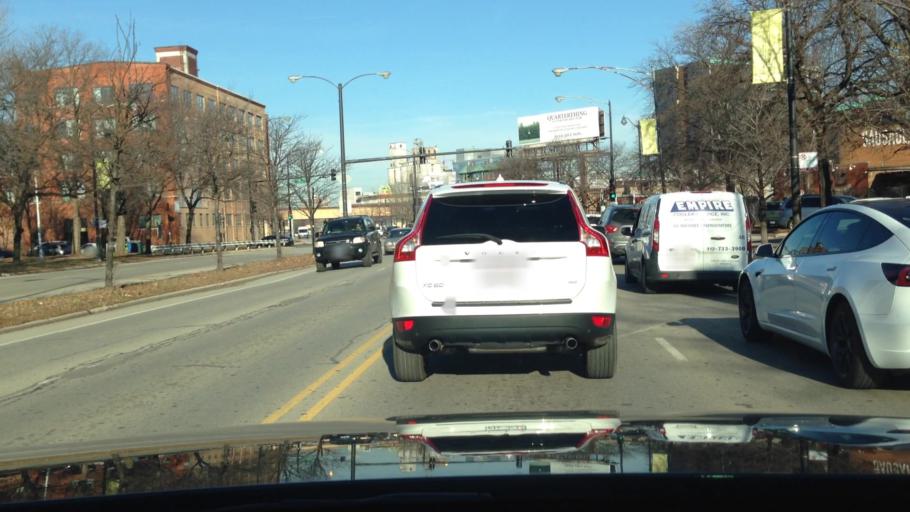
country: US
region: Illinois
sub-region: Cook County
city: Chicago
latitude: 41.8834
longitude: -87.6640
